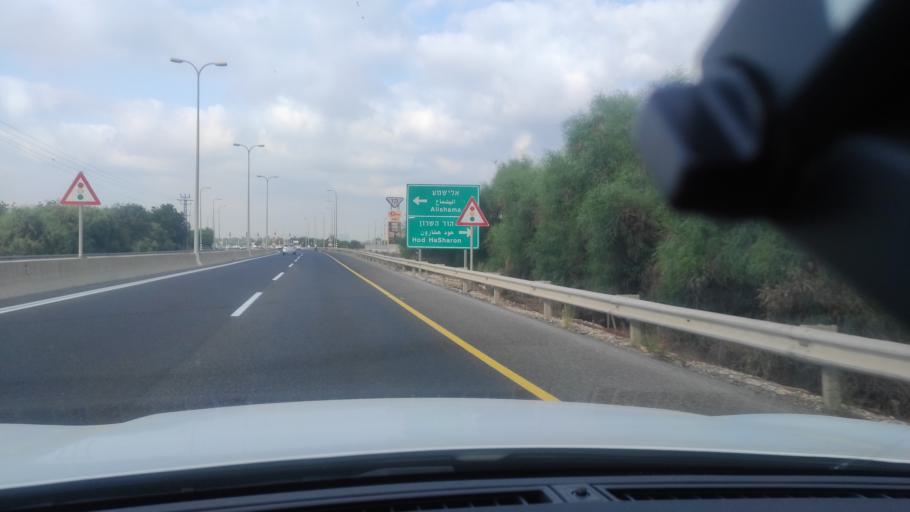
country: IL
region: Central District
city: Kfar Saba
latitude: 32.1540
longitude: 34.9231
